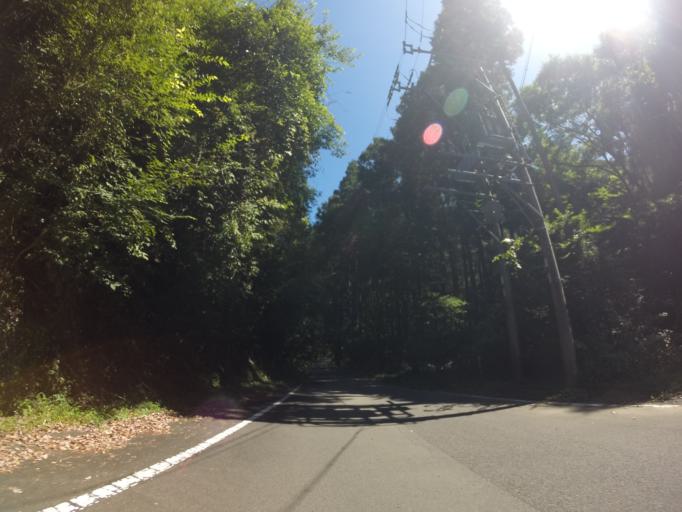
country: JP
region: Shizuoka
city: Fujieda
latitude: 34.9663
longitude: 138.1913
